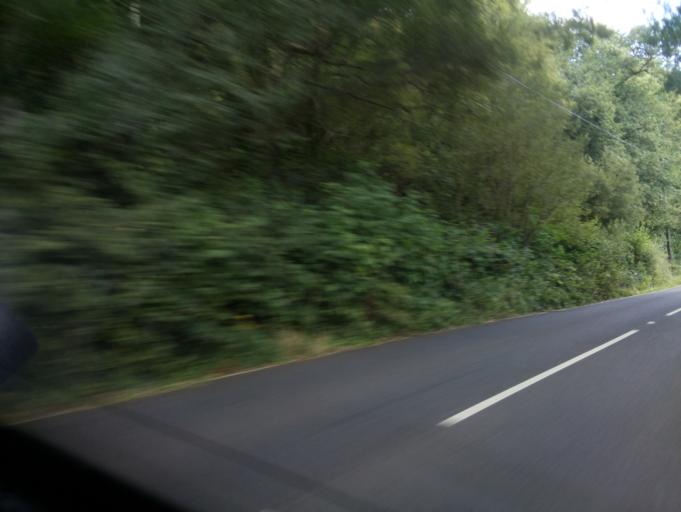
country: GB
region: England
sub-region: Devon
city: Ottery St Mary
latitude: 50.7418
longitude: -3.2098
